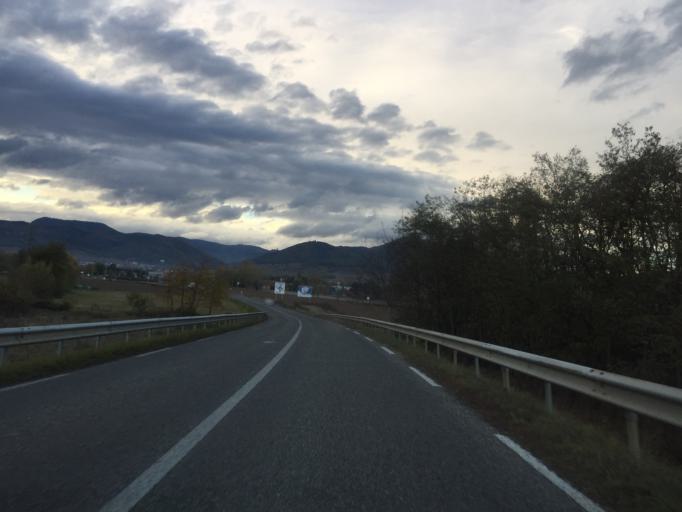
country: FR
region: Alsace
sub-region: Departement du Haut-Rhin
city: Bergheim
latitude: 48.1896
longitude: 7.3757
